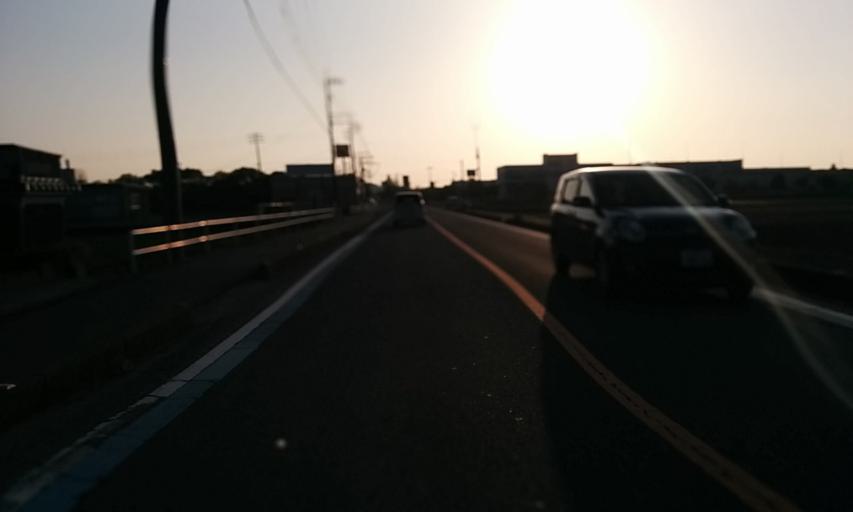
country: JP
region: Ehime
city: Masaki-cho
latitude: 33.7717
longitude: 132.7208
